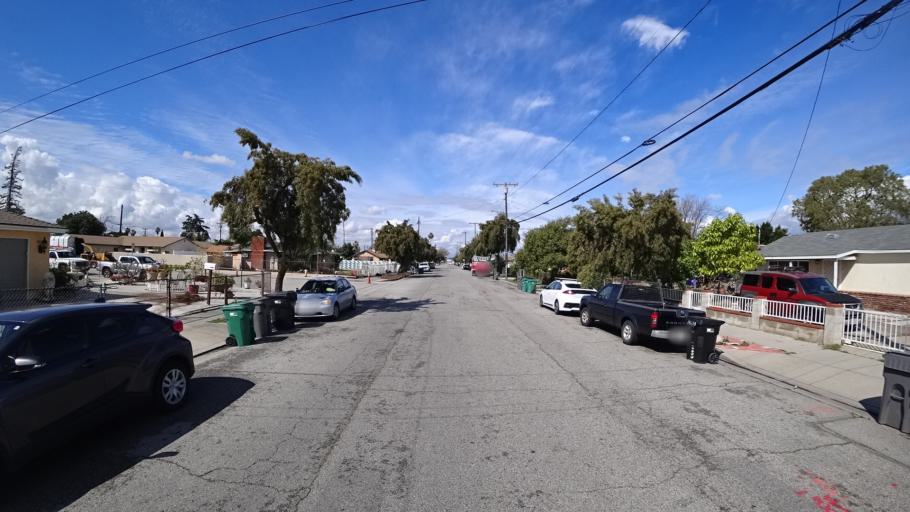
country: US
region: California
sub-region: Los Angeles County
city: Baldwin Park
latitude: 34.0885
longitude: -117.9767
